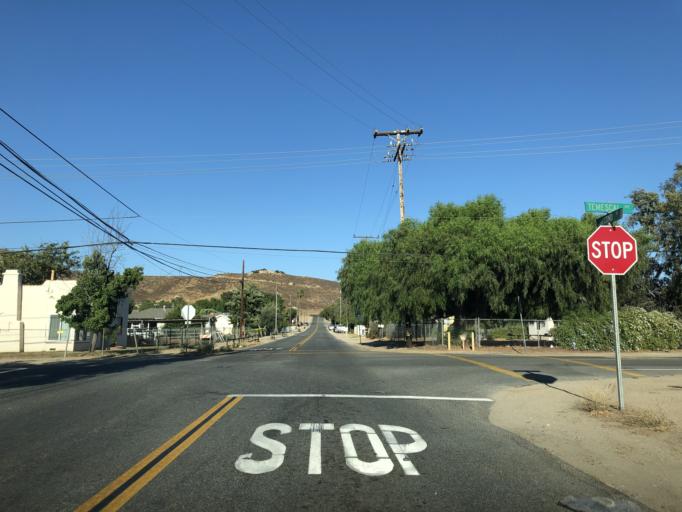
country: US
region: California
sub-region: Riverside County
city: Norco
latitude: 33.9095
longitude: -117.5486
